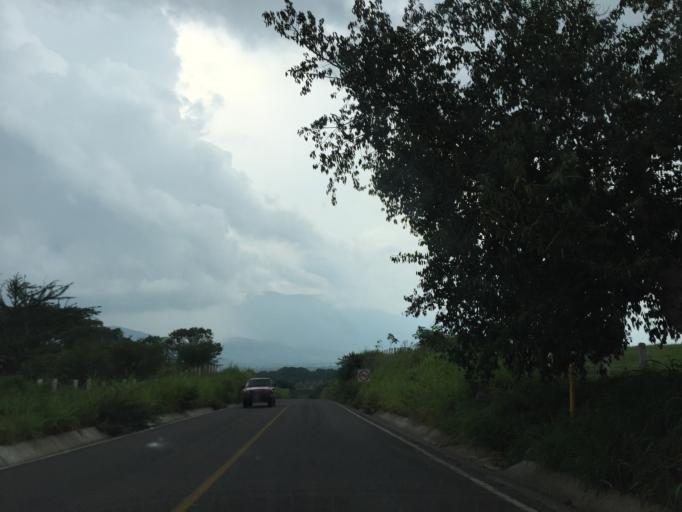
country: MX
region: Colima
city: Comala
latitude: 19.3341
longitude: -103.7682
